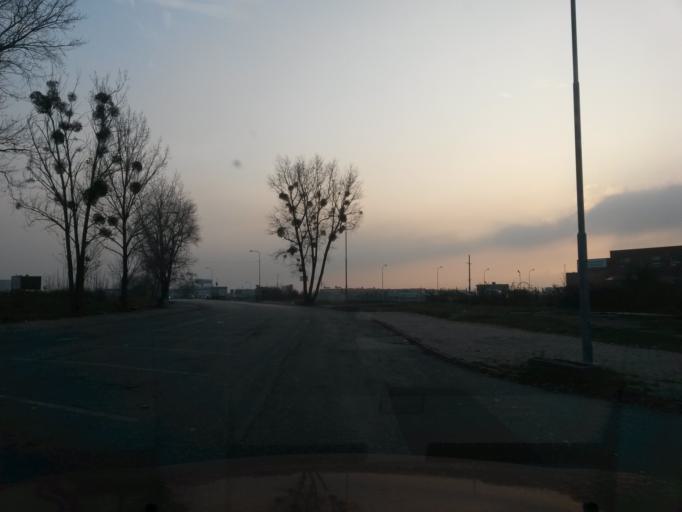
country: SK
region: Kosicky
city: Kosice
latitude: 48.6989
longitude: 21.2483
